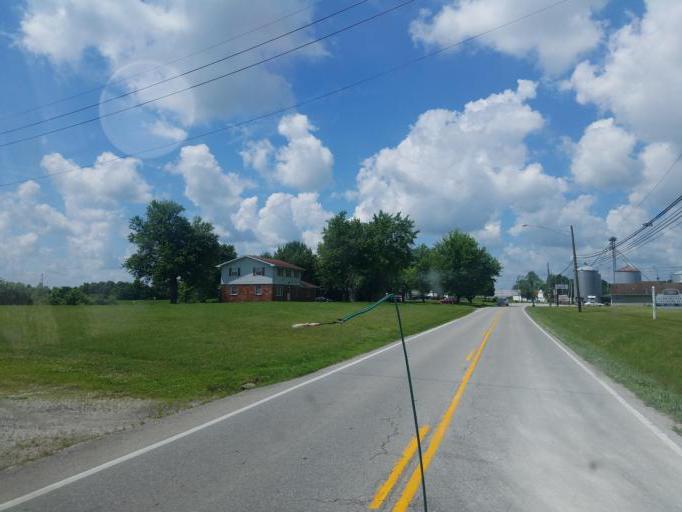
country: US
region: Kentucky
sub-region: Grayson County
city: Leitchfield
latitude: 37.4925
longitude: -86.2414
